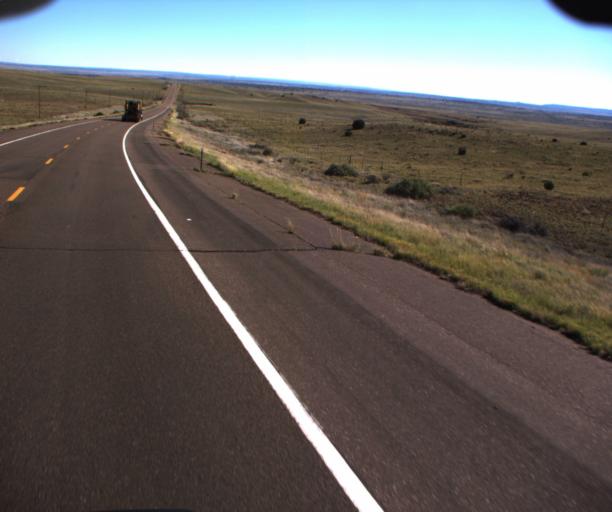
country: US
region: Arizona
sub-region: Apache County
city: Saint Johns
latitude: 34.5014
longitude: -109.4892
